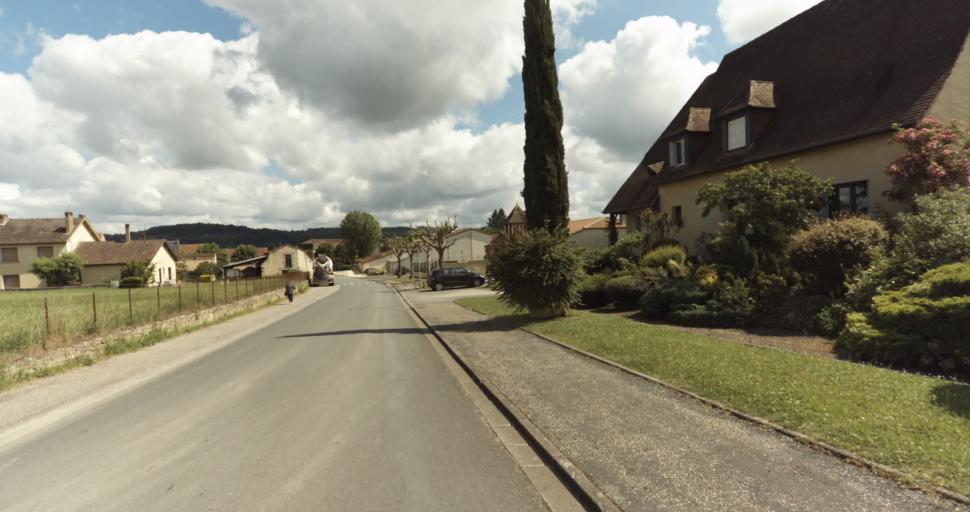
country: FR
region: Aquitaine
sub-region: Departement de la Dordogne
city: Le Bugue
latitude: 44.8446
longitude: 0.9116
